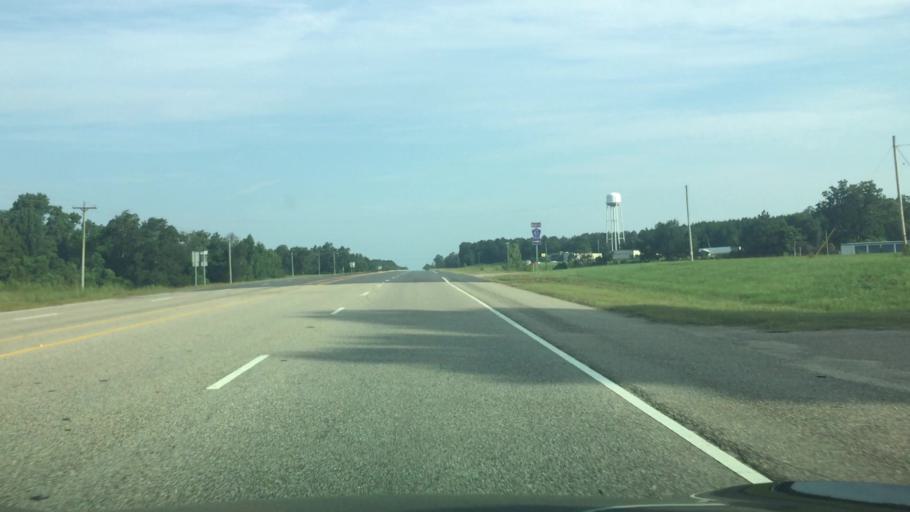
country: US
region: Alabama
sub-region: Butler County
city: Georgiana
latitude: 31.5274
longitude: -86.7186
